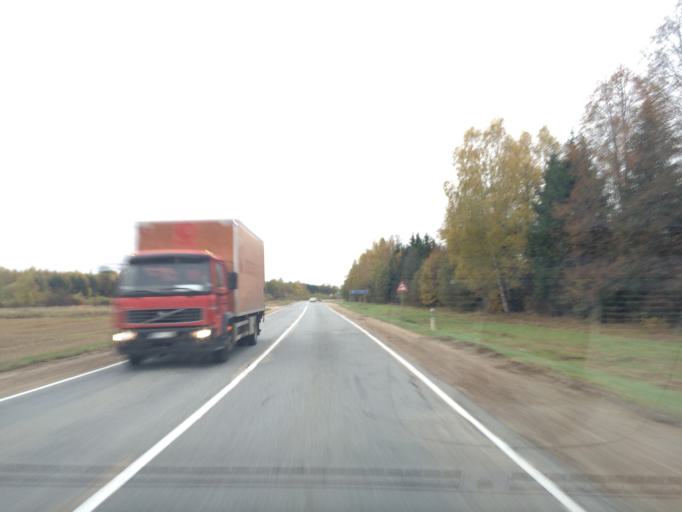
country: LV
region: Plavinu
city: Plavinas
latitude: 56.6026
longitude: 25.7817
